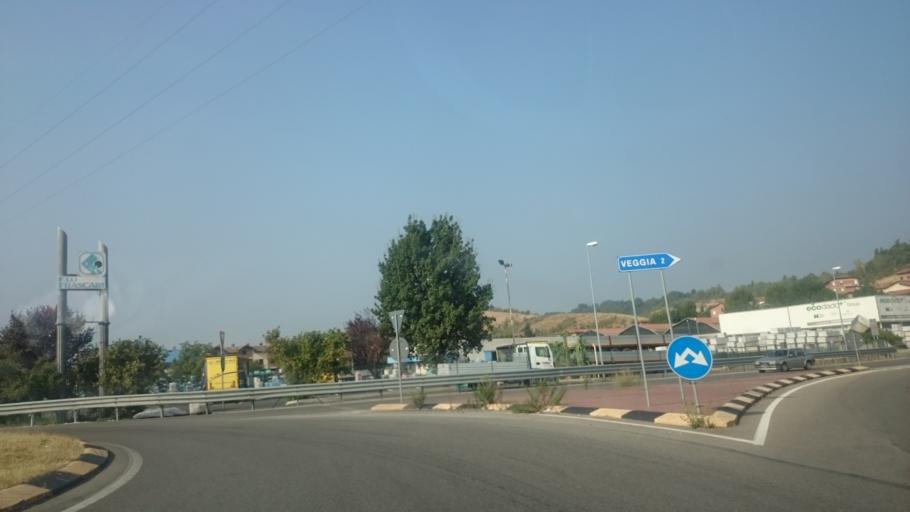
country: IT
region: Emilia-Romagna
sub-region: Provincia di Reggio Emilia
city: Veggia-Villalunga
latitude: 44.5411
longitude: 10.7634
